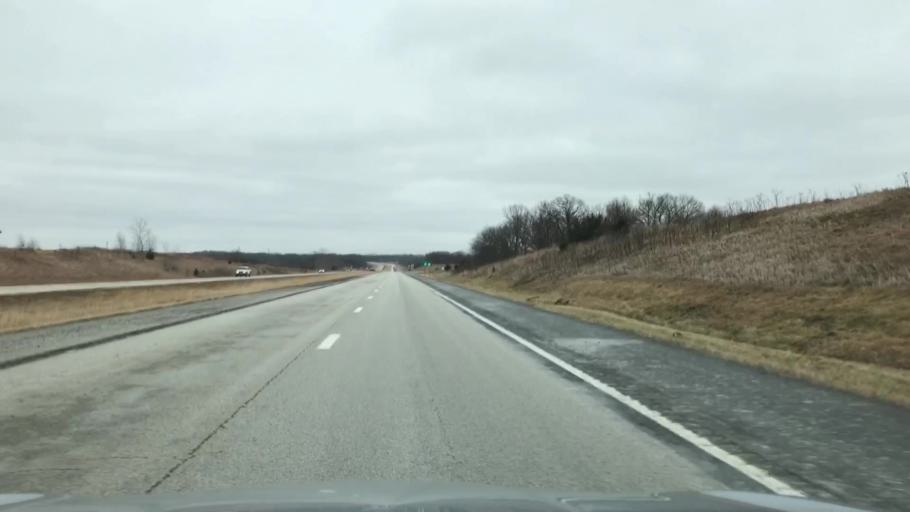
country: US
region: Missouri
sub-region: Caldwell County
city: Hamilton
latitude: 39.7451
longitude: -94.0447
